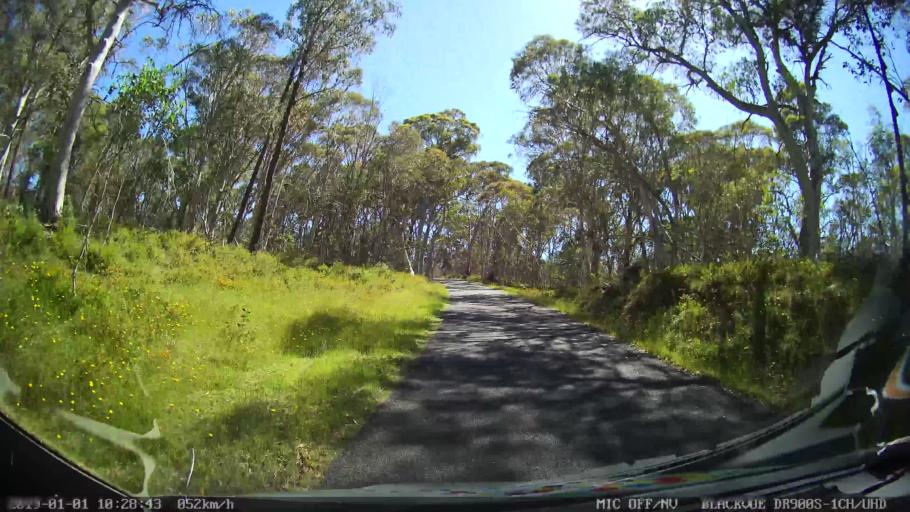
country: AU
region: New South Wales
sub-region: Snowy River
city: Jindabyne
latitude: -36.0587
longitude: 148.2428
